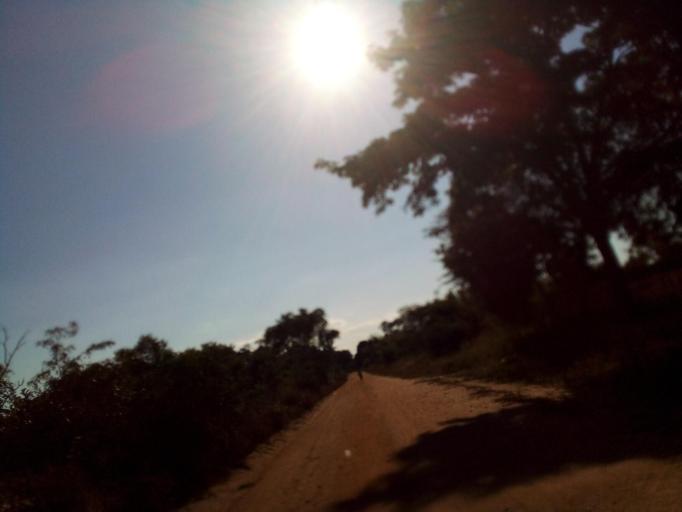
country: MZ
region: Zambezia
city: Quelimane
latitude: -17.5116
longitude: 36.5983
